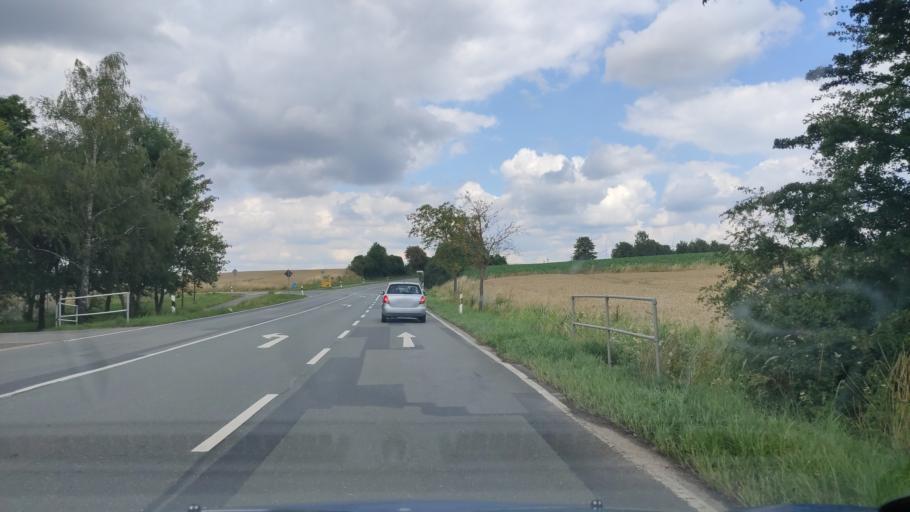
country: DE
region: Lower Saxony
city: Coppenbrugge
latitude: 52.0939
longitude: 9.4942
